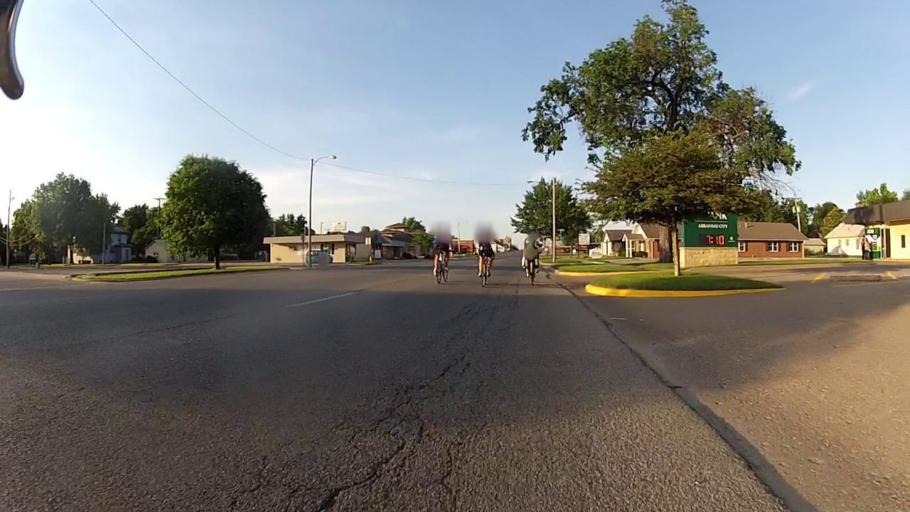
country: US
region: Kansas
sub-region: Cowley County
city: Arkansas City
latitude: 37.0686
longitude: -97.0392
